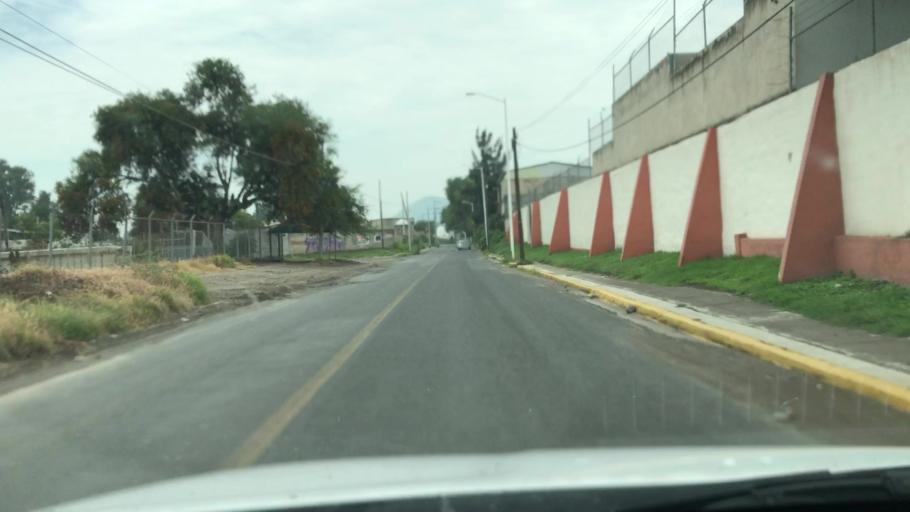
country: MX
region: Jalisco
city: Nicolas R Casillas
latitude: 20.5475
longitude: -103.4735
